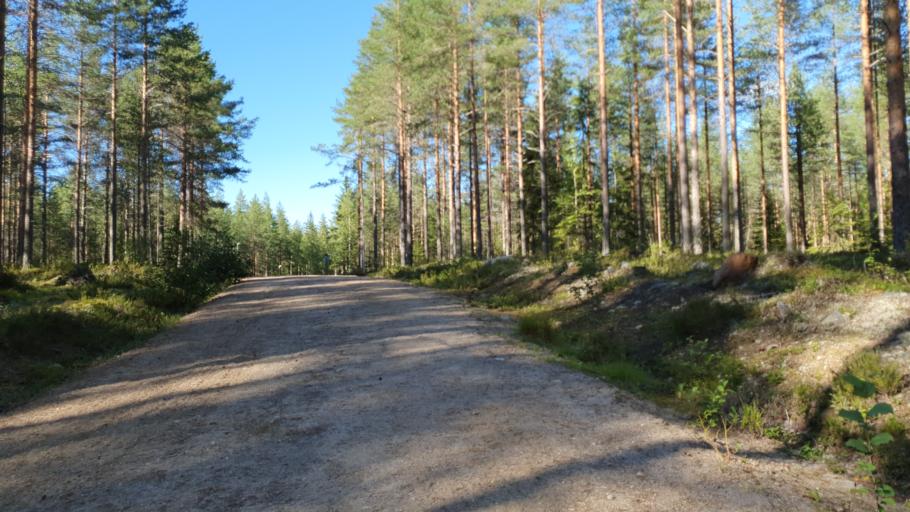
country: FI
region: Kainuu
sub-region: Kehys-Kainuu
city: Kuhmo
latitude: 64.1090
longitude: 29.5087
